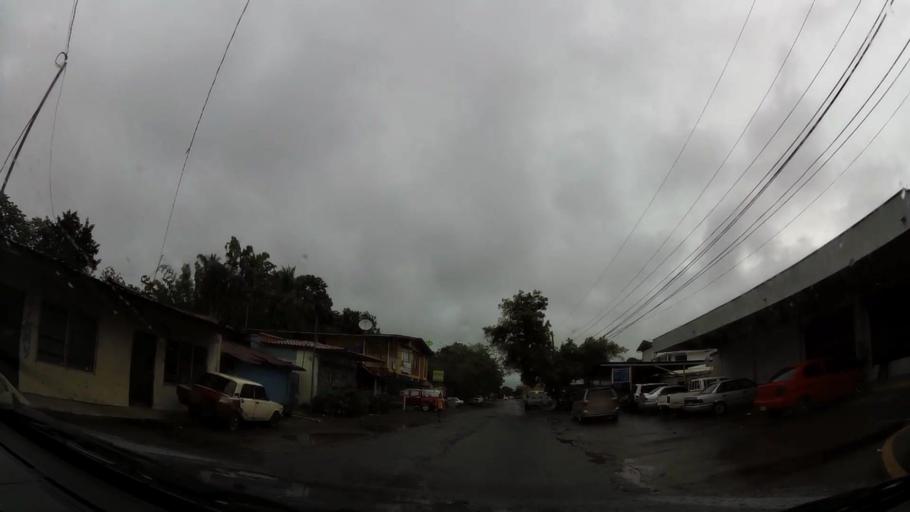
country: PA
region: Chiriqui
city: David
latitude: 8.4291
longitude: -82.4320
